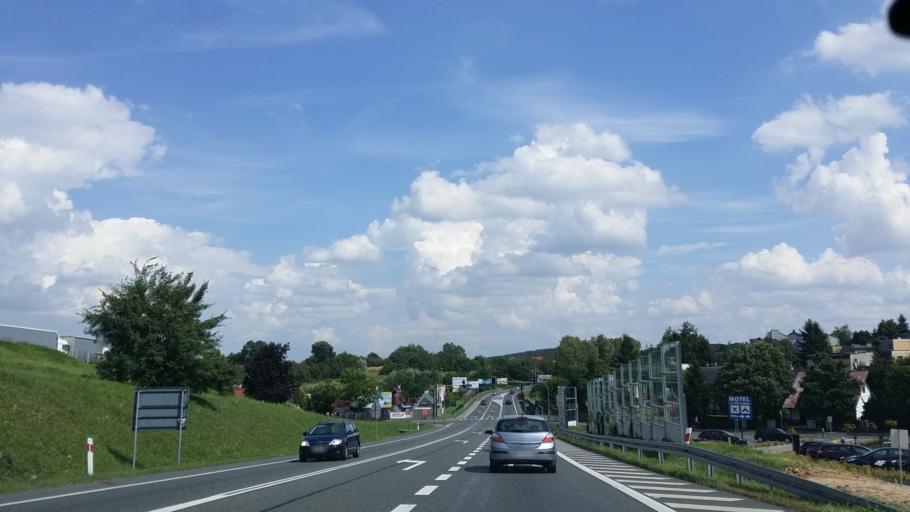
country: PL
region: Lesser Poland Voivodeship
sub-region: Powiat wielicki
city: Wieliczka
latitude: 49.9942
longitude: 20.0721
